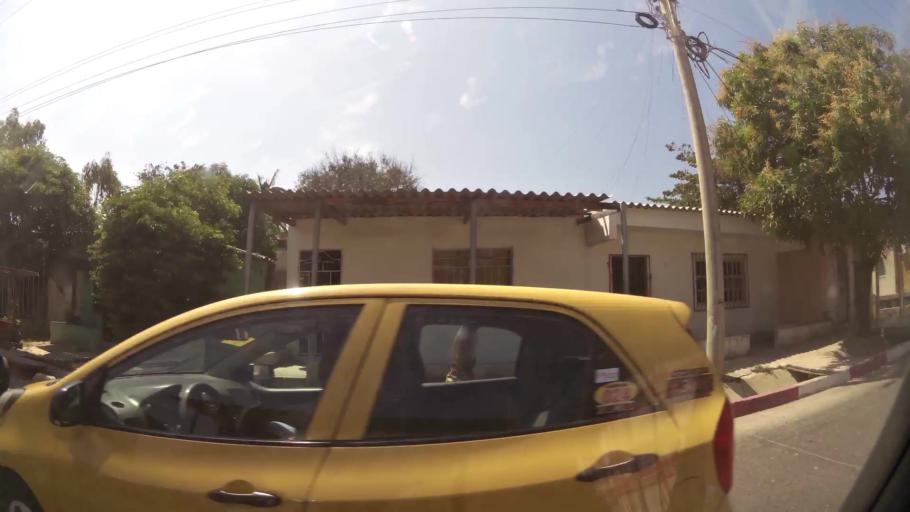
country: CO
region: Atlantico
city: Barranquilla
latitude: 10.9654
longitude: -74.8287
